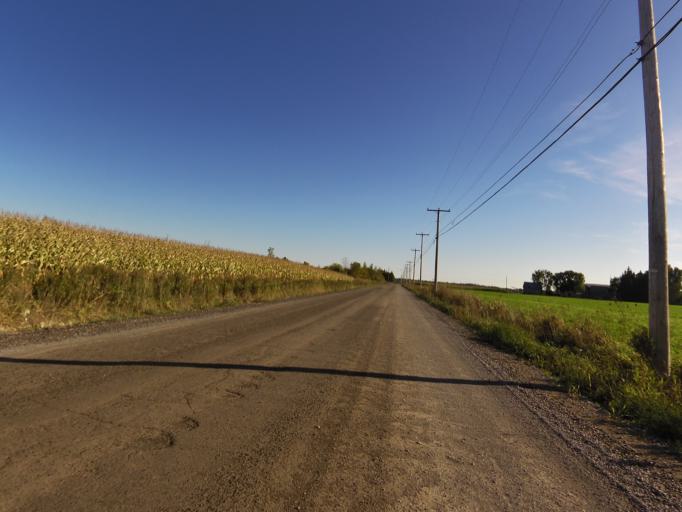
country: CA
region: Ontario
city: Bells Corners
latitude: 45.4794
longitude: -75.8803
